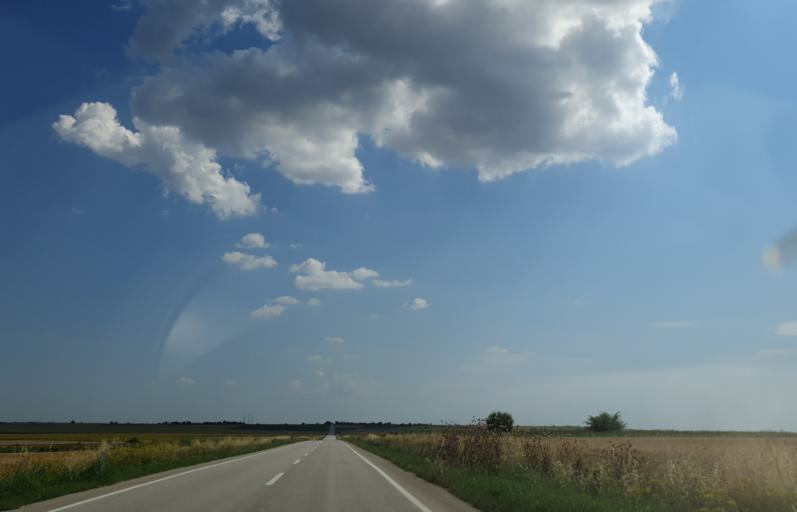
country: TR
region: Kirklareli
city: Buyukkaristiran
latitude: 41.3962
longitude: 27.5732
